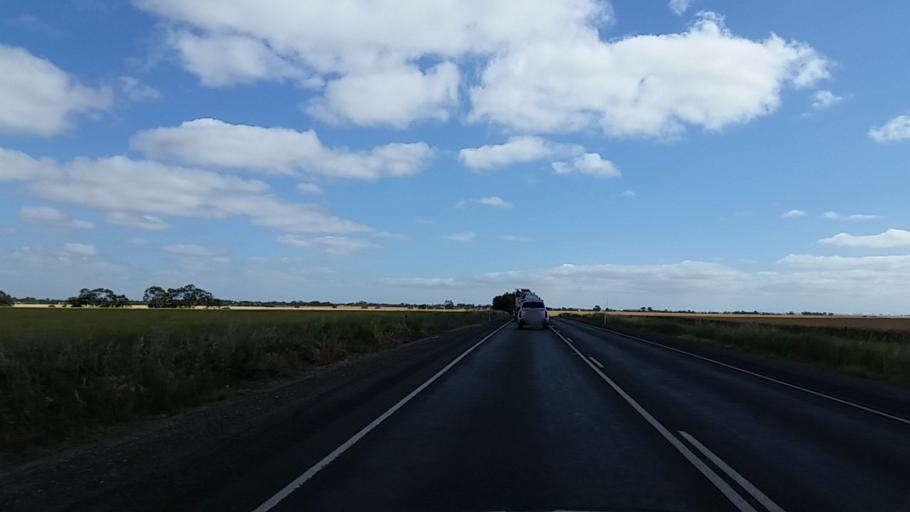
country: AU
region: South Australia
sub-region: Light
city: Willaston
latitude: -34.5615
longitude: 138.7470
